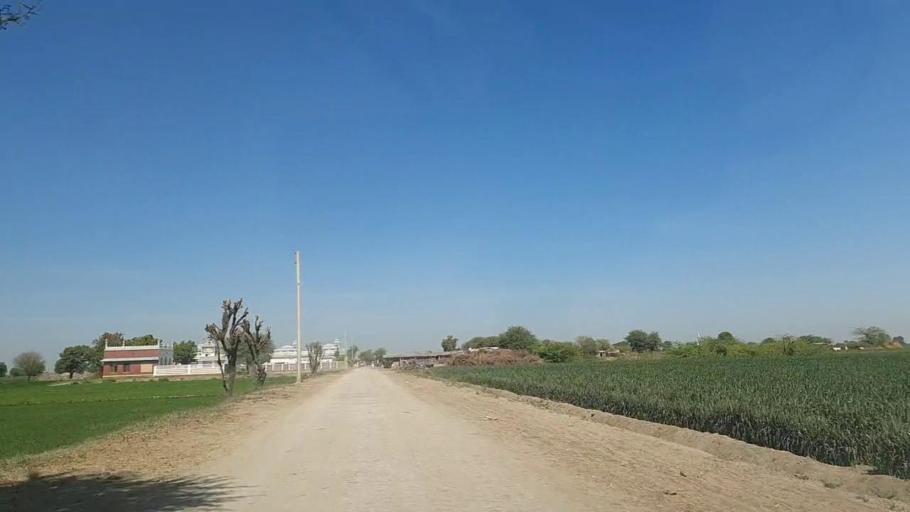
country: PK
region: Sindh
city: Samaro
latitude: 25.3289
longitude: 69.4671
